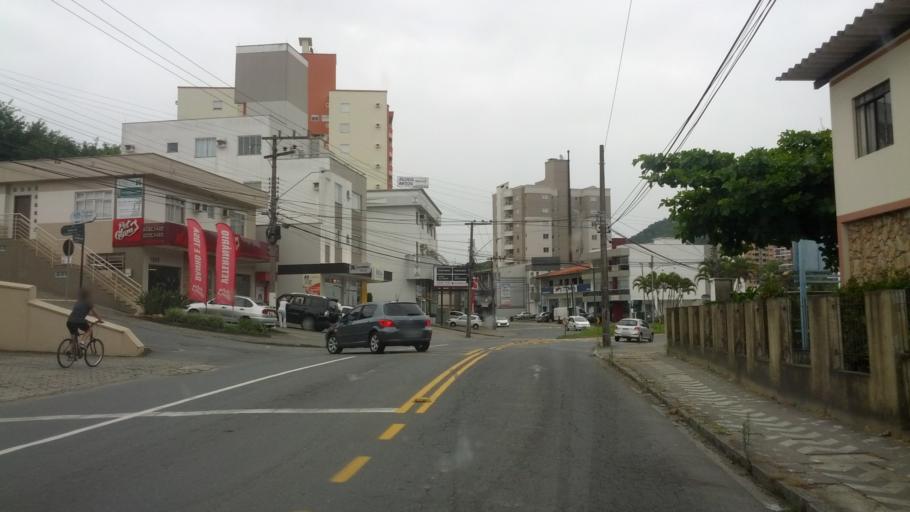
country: BR
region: Santa Catarina
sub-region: Blumenau
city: Blumenau
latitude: -26.9112
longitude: -49.0919
